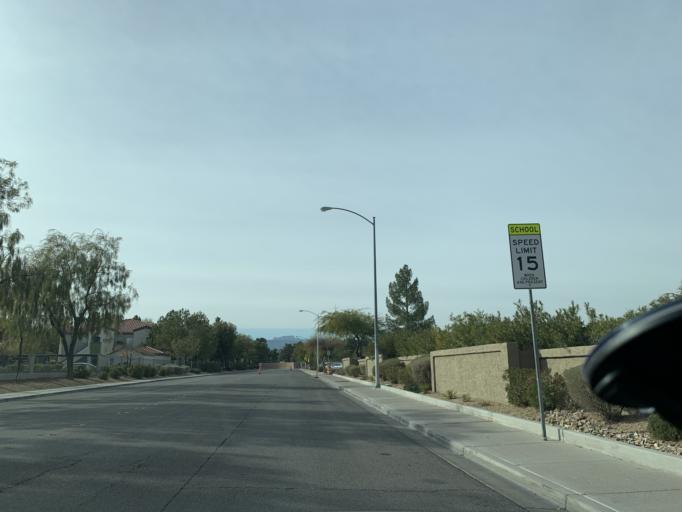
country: US
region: Nevada
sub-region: Clark County
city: Spring Valley
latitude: 36.0962
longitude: -115.2356
